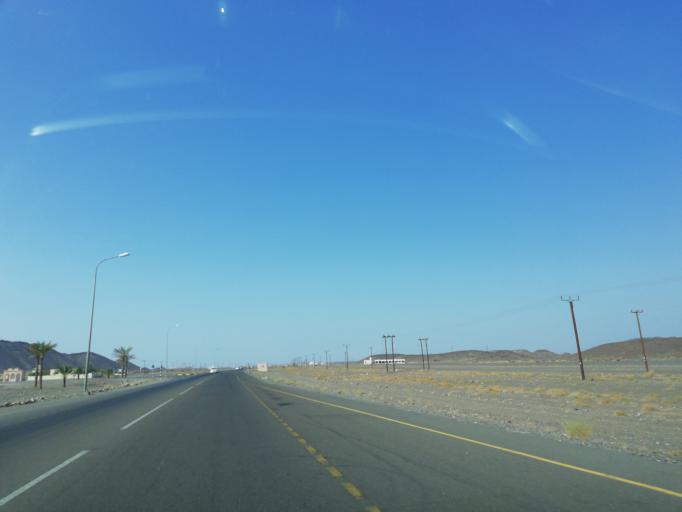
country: OM
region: Ash Sharqiyah
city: Ibra'
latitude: 22.7220
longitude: 58.1488
